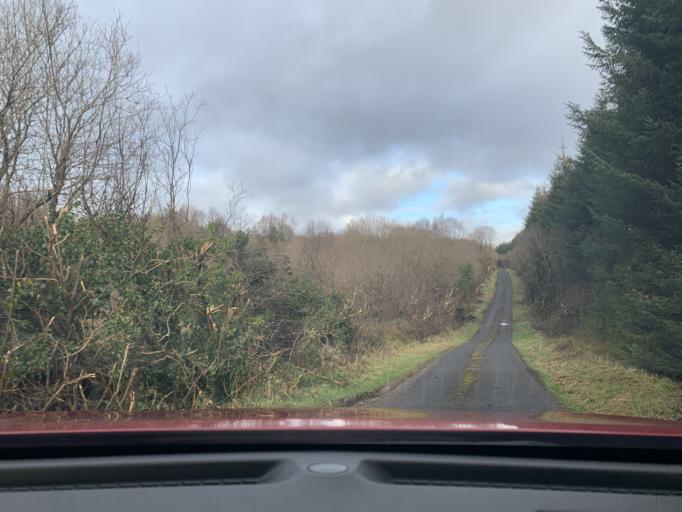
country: IE
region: Connaught
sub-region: Roscommon
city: Ballaghaderreen
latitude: 53.9249
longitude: -8.5638
